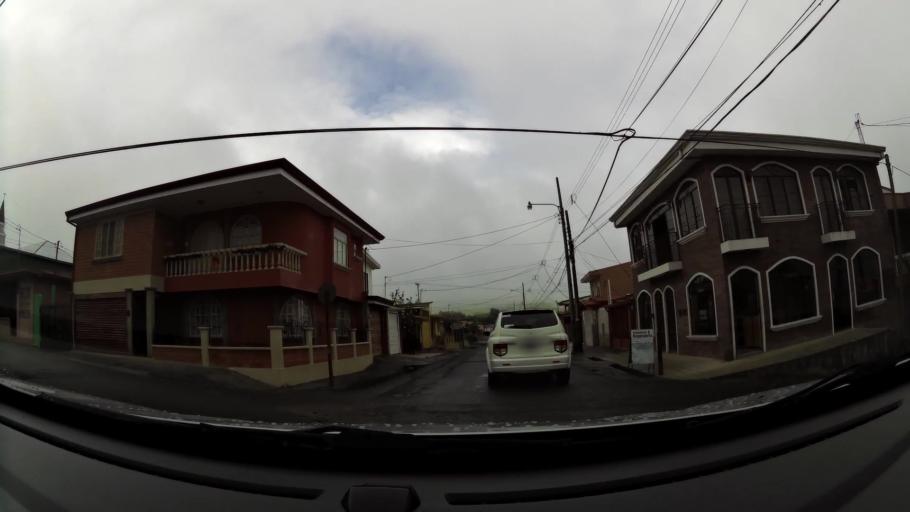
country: CR
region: Cartago
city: Paraiso
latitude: 9.8380
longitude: -83.8640
